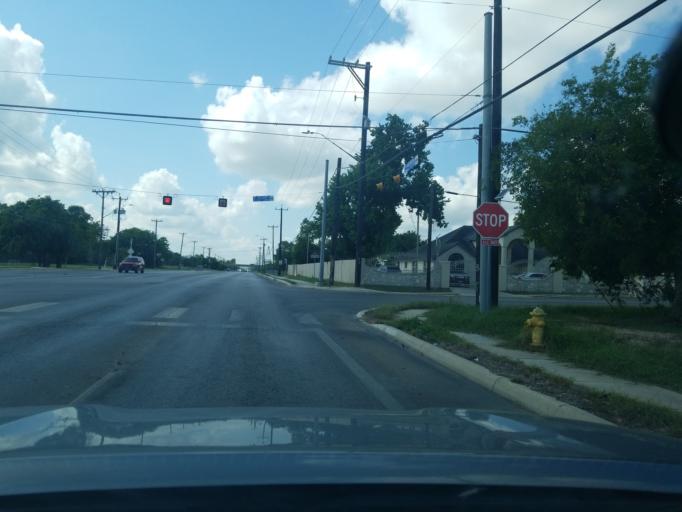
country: US
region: Texas
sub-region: Bexar County
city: Lackland Air Force Base
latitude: 29.3257
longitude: -98.5327
